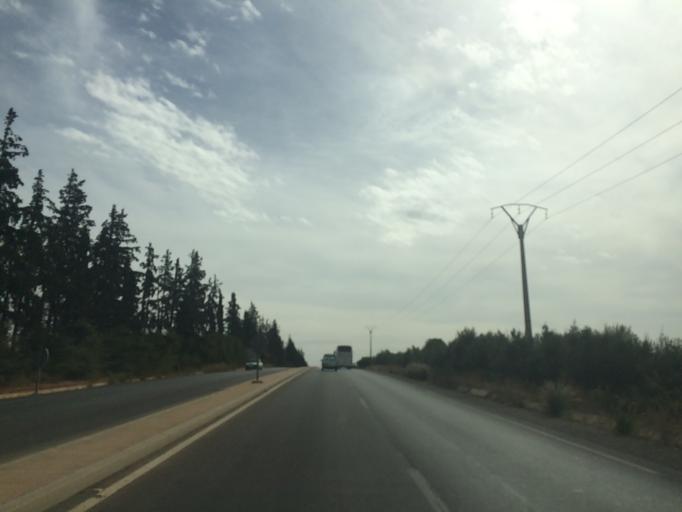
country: MA
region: Meknes-Tafilalet
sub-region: El-Hajeb
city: El Hajeb
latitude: 33.7290
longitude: -5.4657
